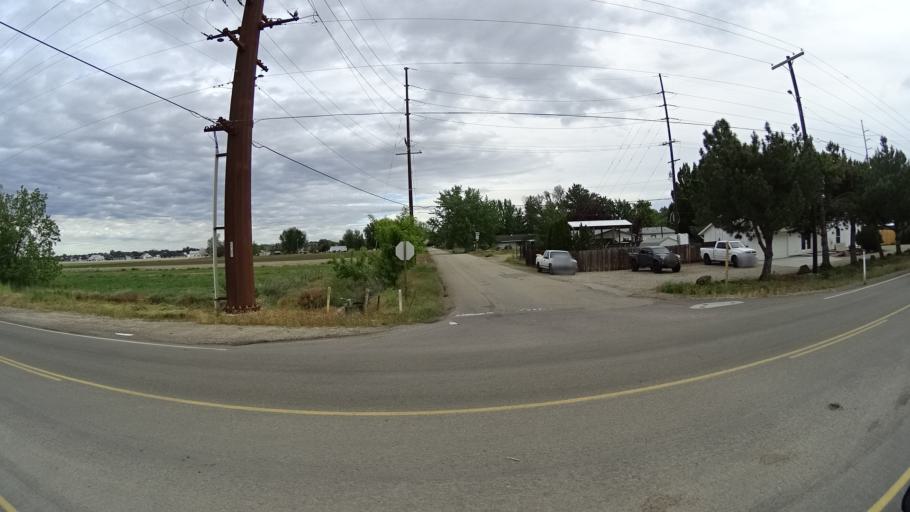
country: US
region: Idaho
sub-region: Ada County
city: Star
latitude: 43.6921
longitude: -116.4984
